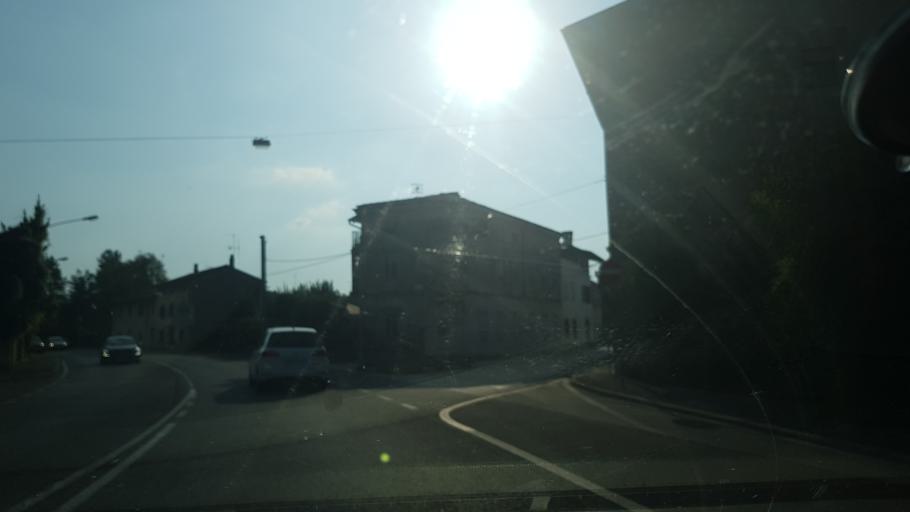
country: IT
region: Friuli Venezia Giulia
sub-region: Provincia di Gorizia
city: Gorizia
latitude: 45.9376
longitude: 13.6320
